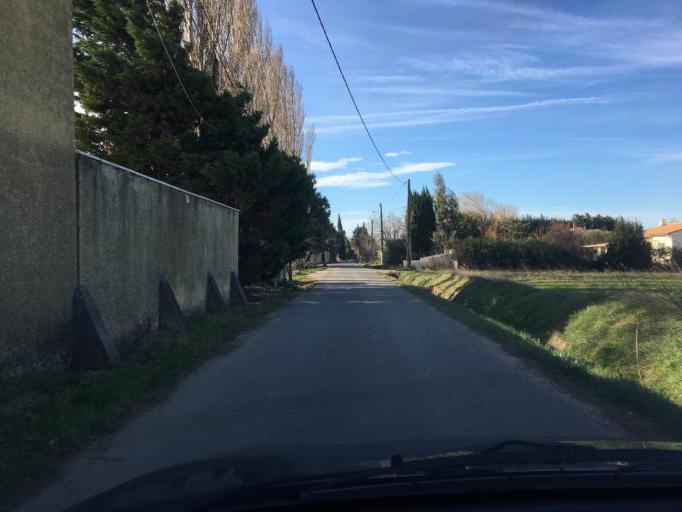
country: FR
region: Provence-Alpes-Cote d'Azur
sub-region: Departement du Vaucluse
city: Jonquieres
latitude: 44.1140
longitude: 4.8886
